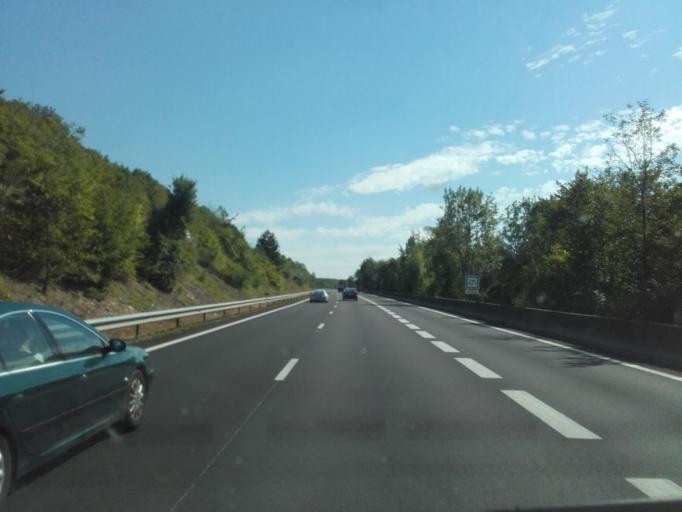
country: FR
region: Bourgogne
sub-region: Departement de la Cote-d'Or
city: Savigny-les-Beaune
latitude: 47.1316
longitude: 4.6990
